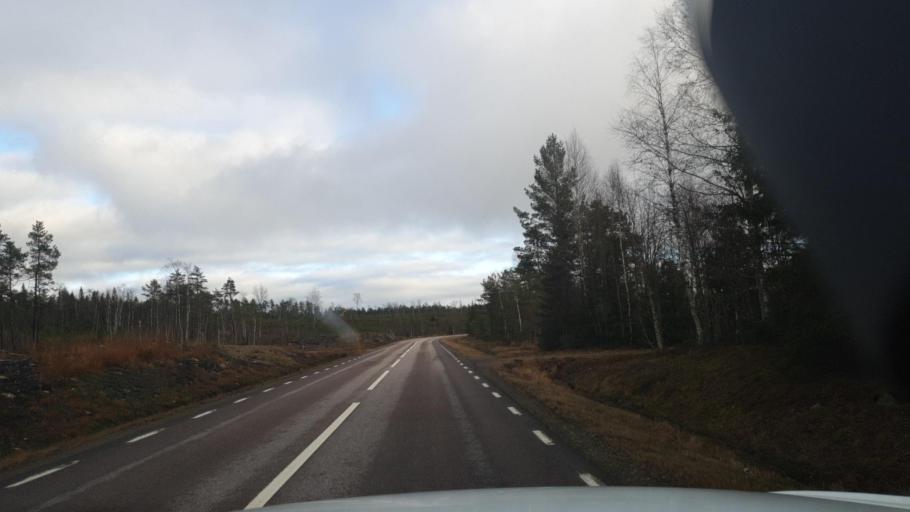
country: SE
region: Vaermland
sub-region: Sunne Kommun
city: Sunne
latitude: 59.6917
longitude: 13.0668
